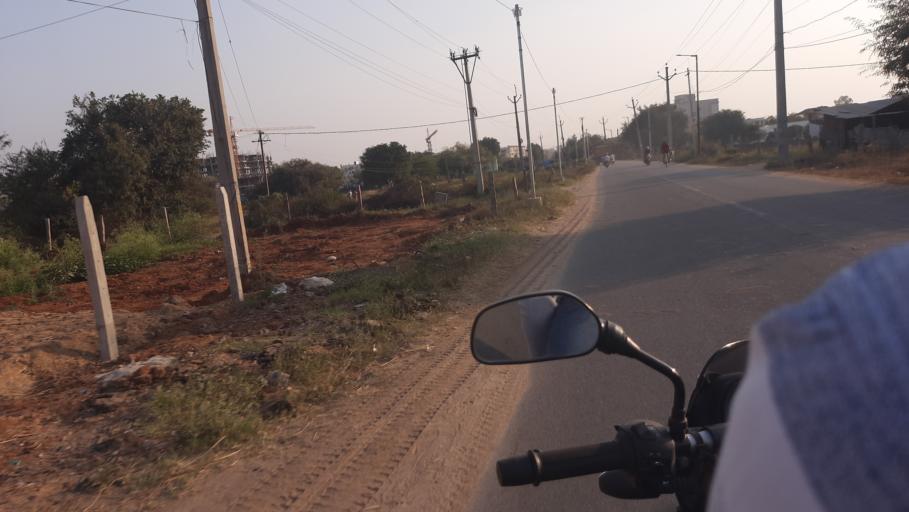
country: IN
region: Telangana
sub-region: Rangareddi
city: Secunderabad
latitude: 17.5254
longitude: 78.5420
